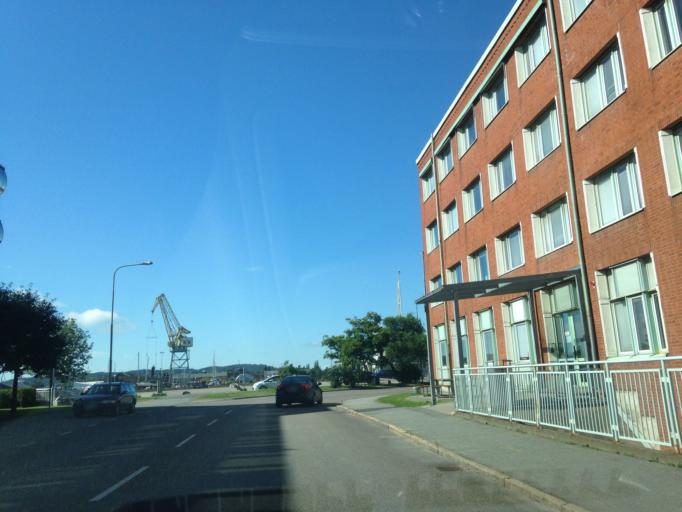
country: SE
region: Vaestra Goetaland
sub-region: Goteborg
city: Goeteborg
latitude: 57.7147
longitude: 11.9723
